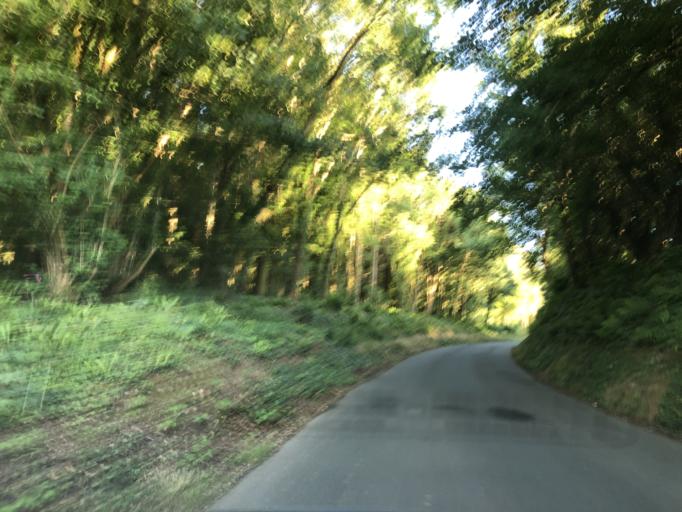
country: GB
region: England
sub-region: Isle of Wight
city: Shalfleet
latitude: 50.6609
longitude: -1.4066
